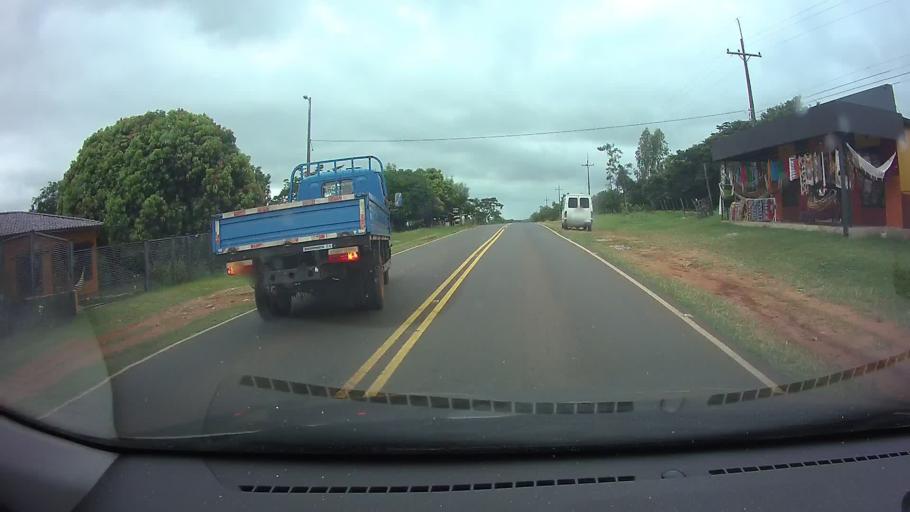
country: PY
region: Paraguari
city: Carapegua
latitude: -25.7265
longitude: -57.3165
